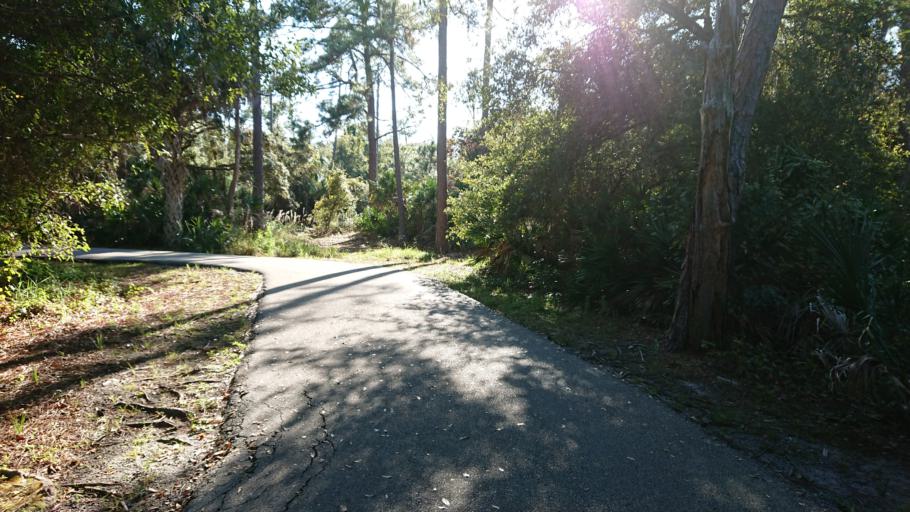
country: US
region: Florida
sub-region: Pinellas County
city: Seminole
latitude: 27.8469
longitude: -82.7755
